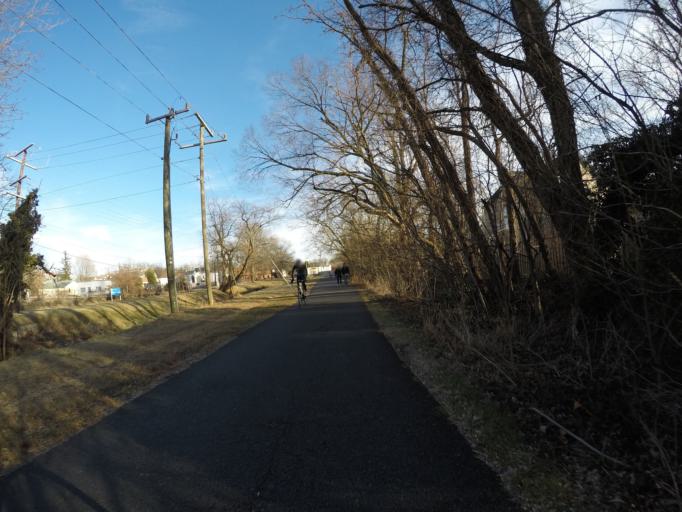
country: US
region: Virginia
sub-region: Loudoun County
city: Leesburg
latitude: 39.1127
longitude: -77.5678
